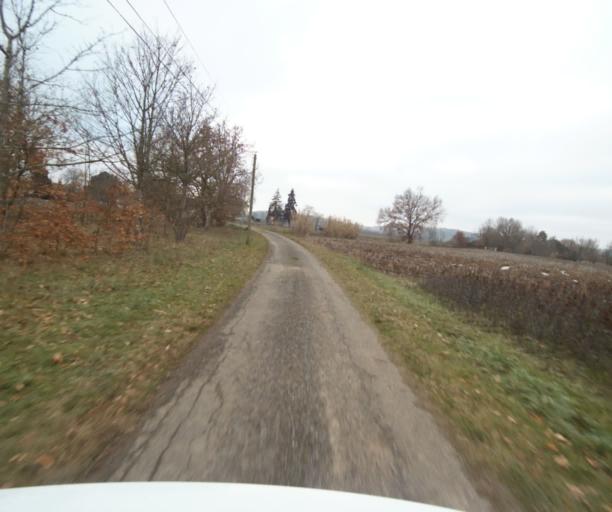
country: FR
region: Midi-Pyrenees
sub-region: Departement du Tarn-et-Garonne
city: Moissac
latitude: 44.1027
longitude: 1.1257
